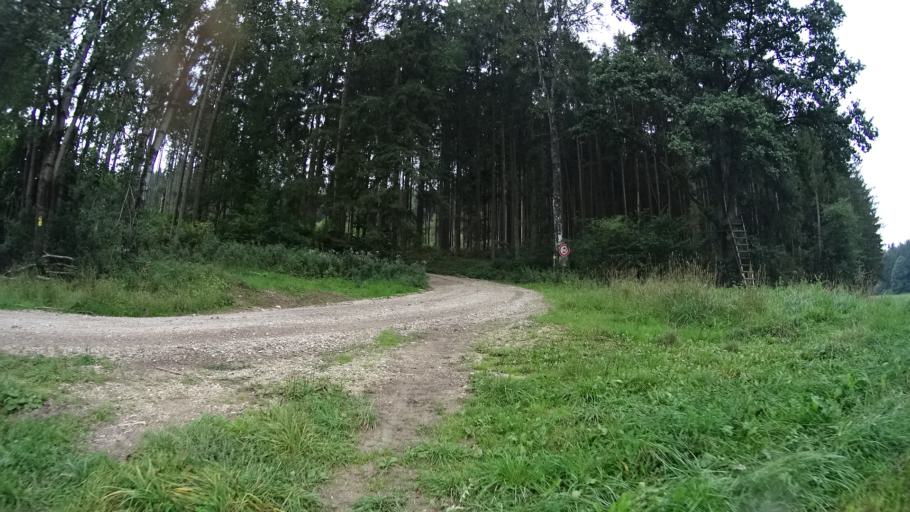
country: DE
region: Bavaria
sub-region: Upper Bavaria
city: Bohmfeld
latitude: 48.8785
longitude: 11.3571
